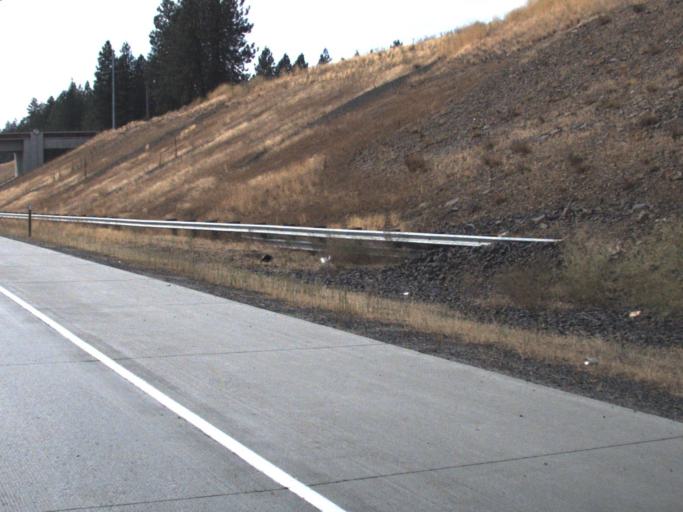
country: US
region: Washington
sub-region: Spokane County
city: Fairwood
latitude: 47.7789
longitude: -117.3873
